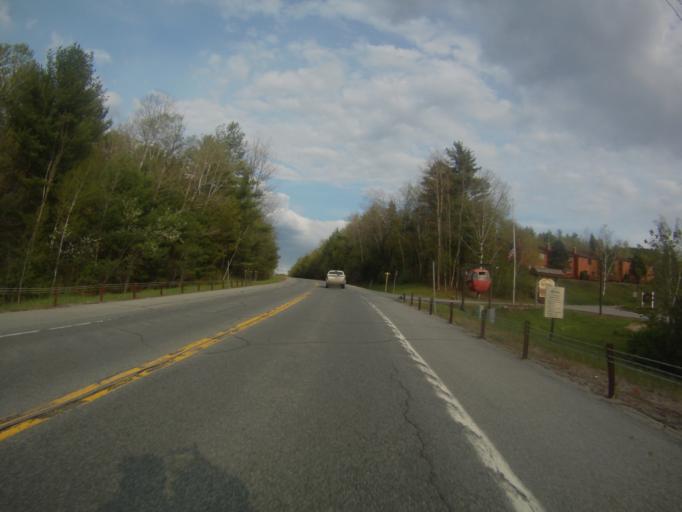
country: US
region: New York
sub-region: Warren County
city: Warrensburg
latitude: 43.6849
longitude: -73.9841
